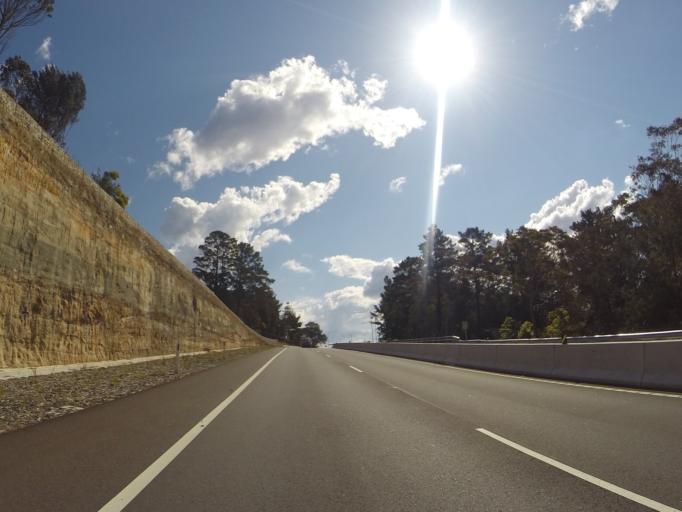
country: AU
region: New South Wales
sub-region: Blue Mountains Municipality
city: Lawson
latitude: -33.7262
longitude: 150.3861
